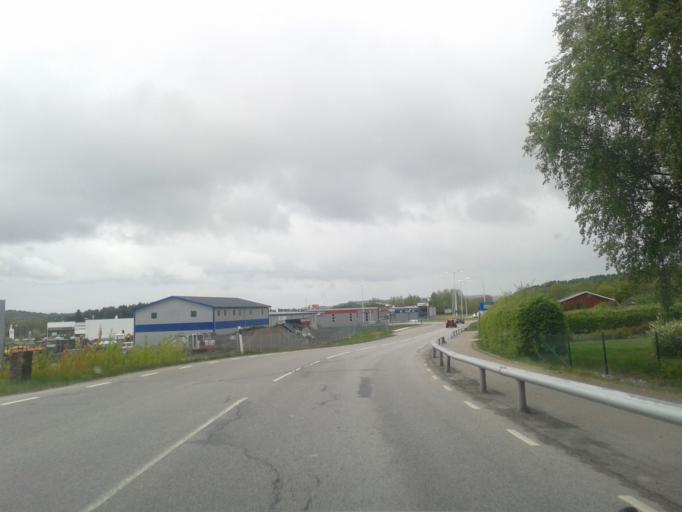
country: SE
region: Vaestra Goetaland
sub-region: Kungalvs Kommun
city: Kungalv
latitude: 57.8898
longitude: 11.9460
